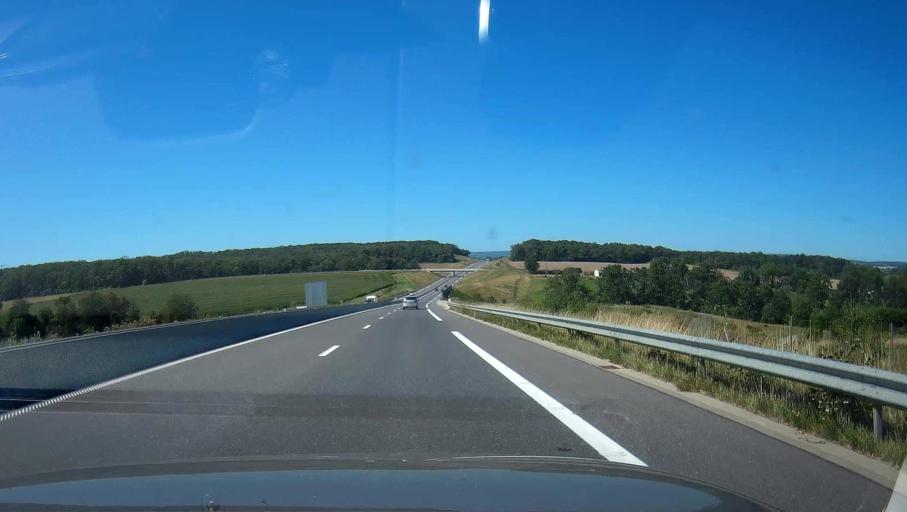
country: FR
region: Champagne-Ardenne
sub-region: Departement des Ardennes
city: Prix-les-Mezieres
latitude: 49.7489
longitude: 4.6648
